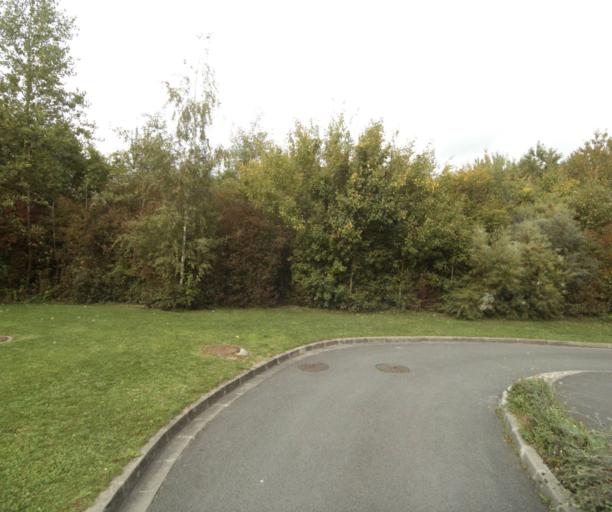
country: FR
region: Nord-Pas-de-Calais
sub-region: Departement du Nord
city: Erquinghem-Lys
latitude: 50.6770
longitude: 2.8379
